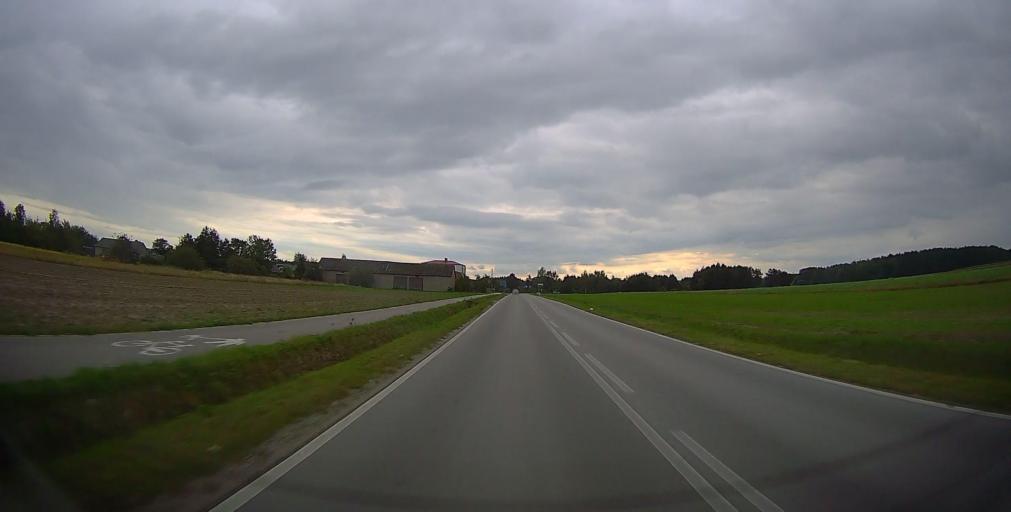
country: PL
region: Masovian Voivodeship
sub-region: Powiat radomski
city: Zakrzew
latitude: 51.4394
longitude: 21.0532
